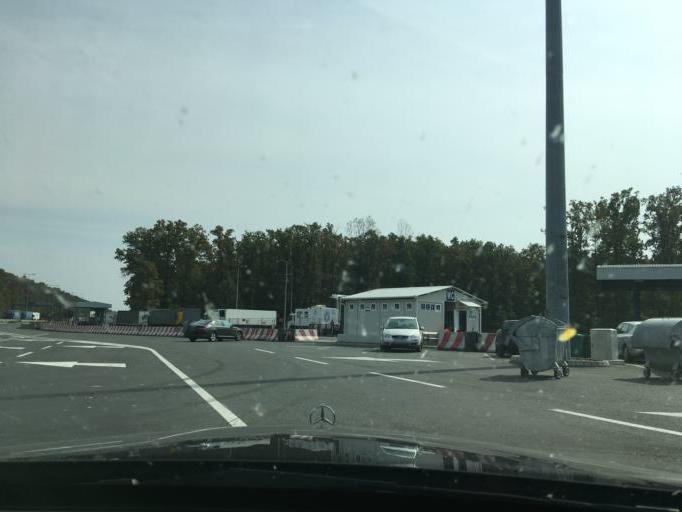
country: HR
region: Vukovarsko-Srijemska
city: Nijemci
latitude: 45.0470
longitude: 19.1078
